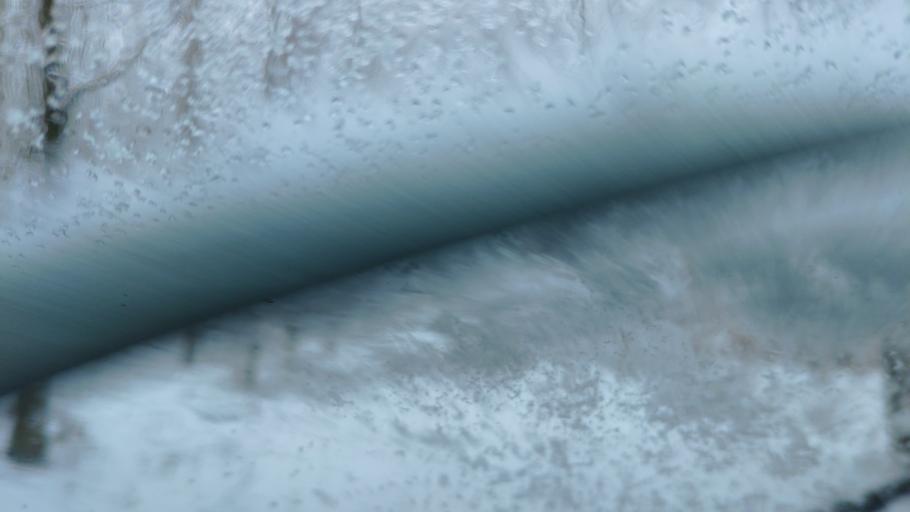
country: SK
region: Kosicky
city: Kosice
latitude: 48.6565
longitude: 21.1816
